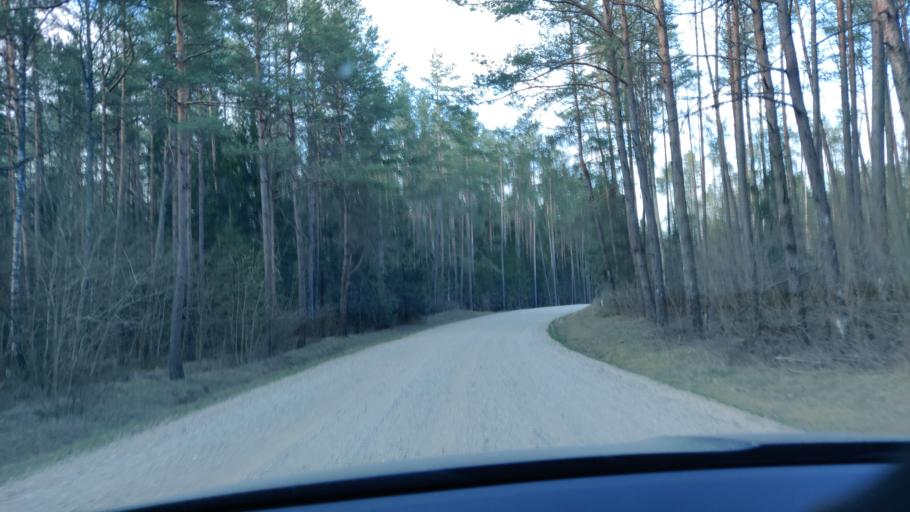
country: LT
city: Trakai
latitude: 54.5762
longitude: 24.9687
